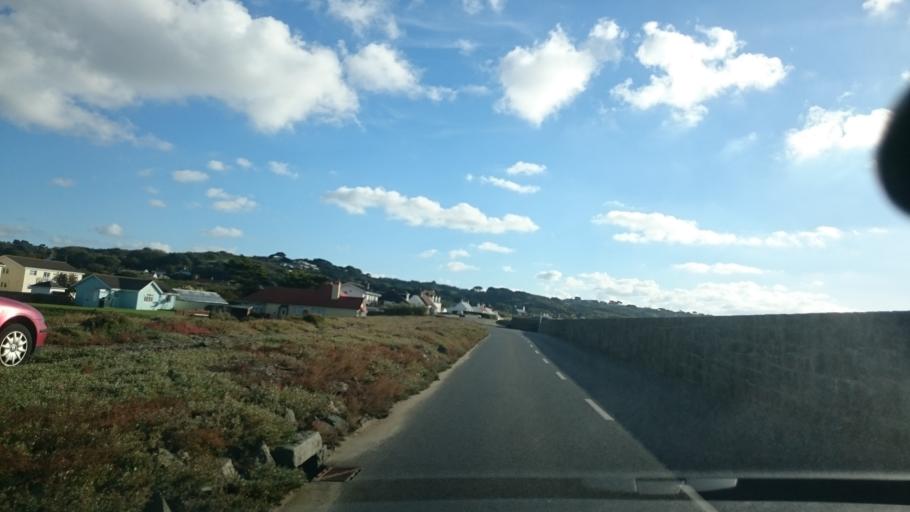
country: GG
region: St Peter Port
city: Saint Peter Port
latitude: 49.4476
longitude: -2.6494
